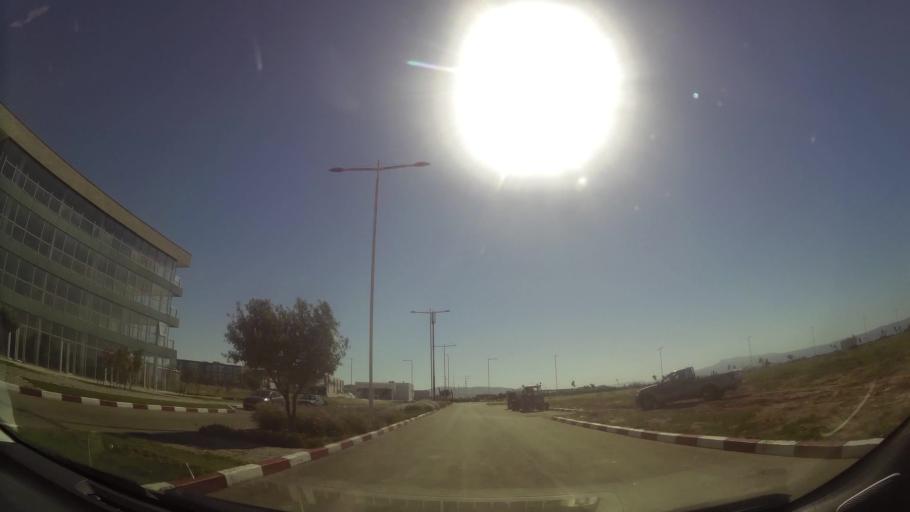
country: MA
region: Oriental
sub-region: Oujda-Angad
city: Oujda
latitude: 34.7706
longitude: -1.9370
